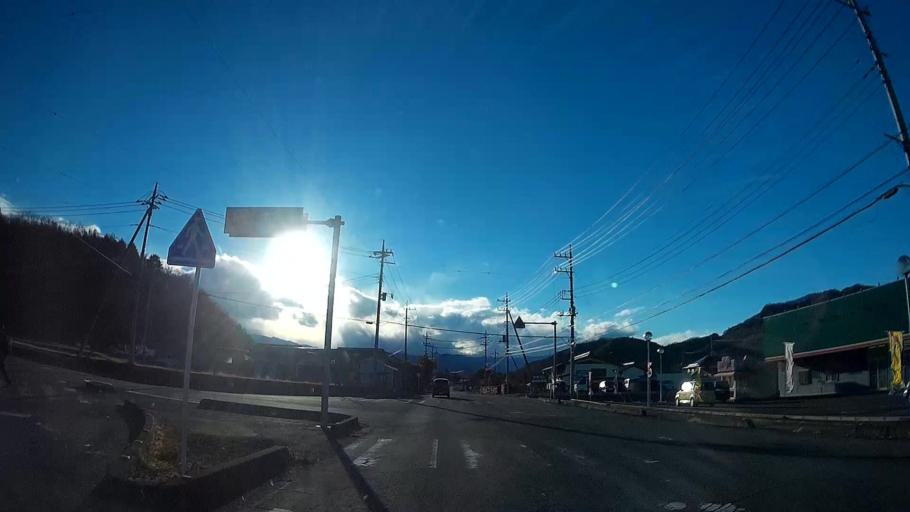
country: JP
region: Saitama
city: Chichibu
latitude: 36.0535
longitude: 139.0559
